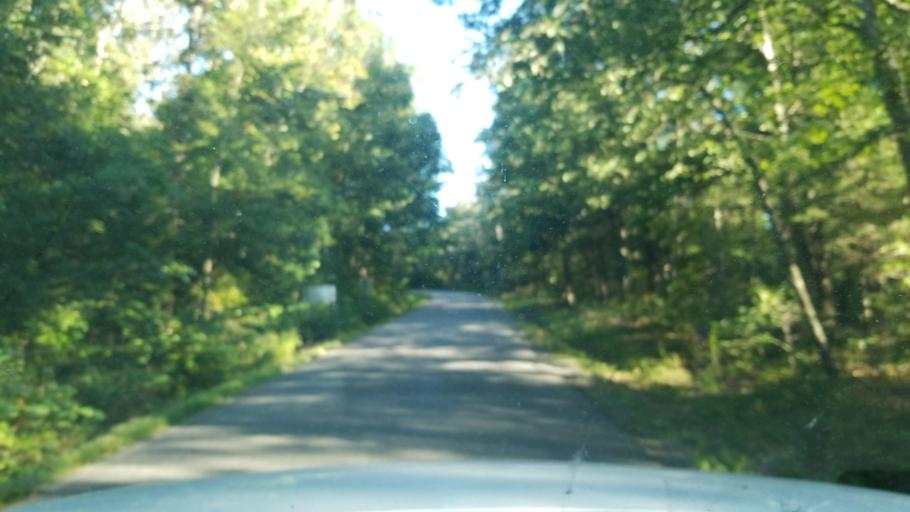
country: US
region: Illinois
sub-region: Hardin County
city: Elizabethtown
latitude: 37.6022
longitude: -88.3829
